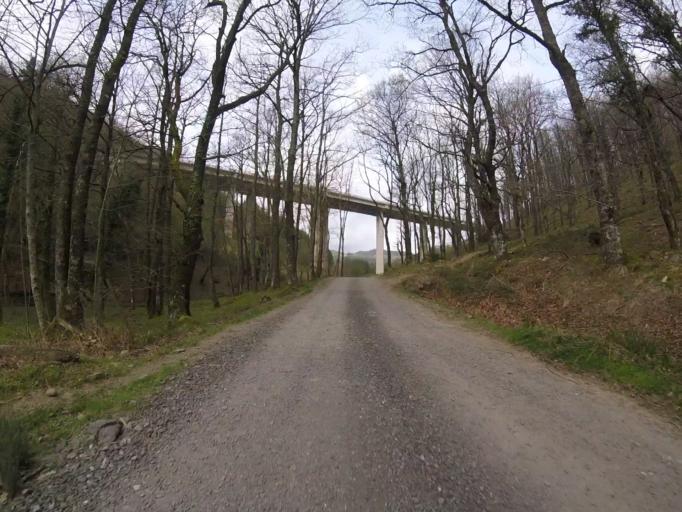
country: ES
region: Navarre
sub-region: Provincia de Navarra
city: Areso
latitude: 43.1070
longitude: -1.9500
